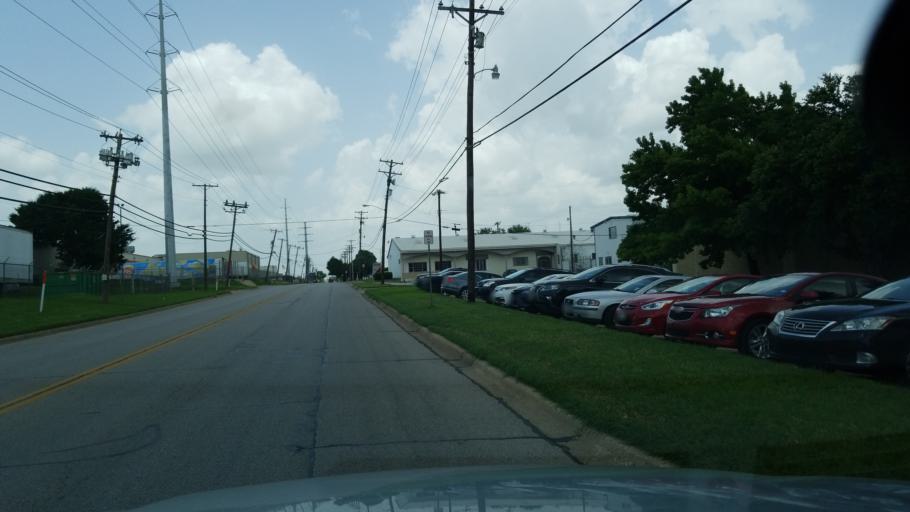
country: US
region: Texas
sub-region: Dallas County
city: Irving
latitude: 32.8190
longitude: -96.9168
